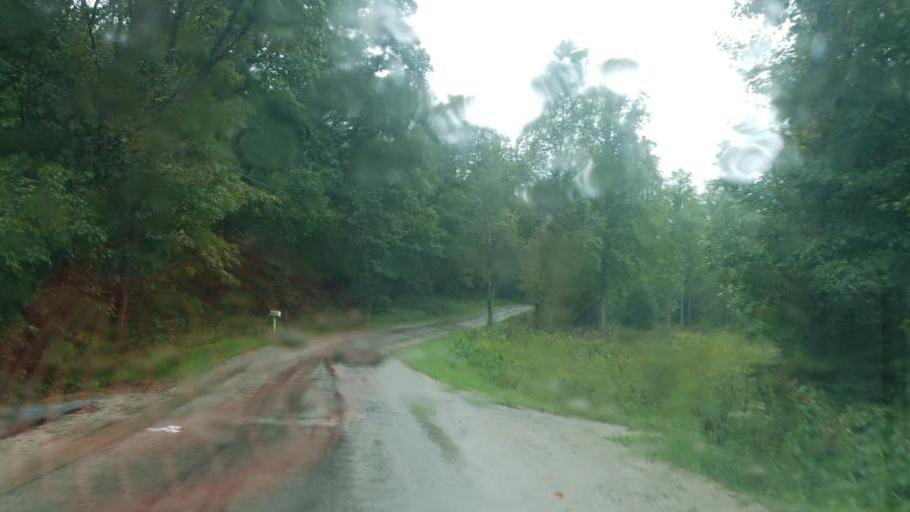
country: US
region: Kentucky
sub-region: Lewis County
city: Vanceburg
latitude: 38.7842
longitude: -83.2589
